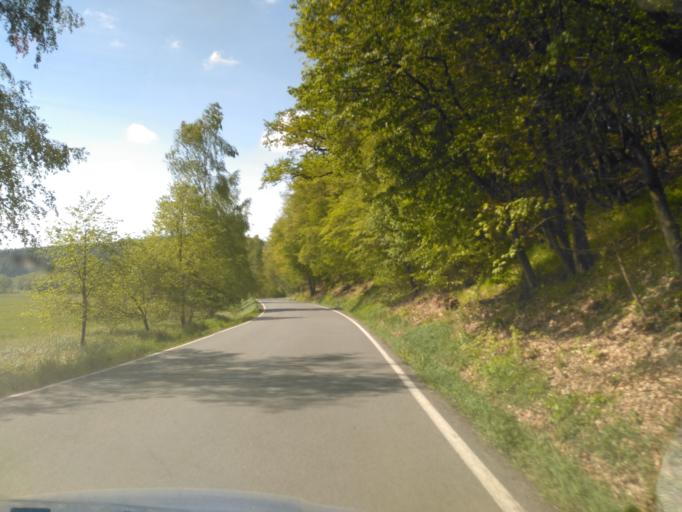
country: CZ
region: Central Bohemia
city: Lochovice
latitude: 49.8377
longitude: 13.9696
